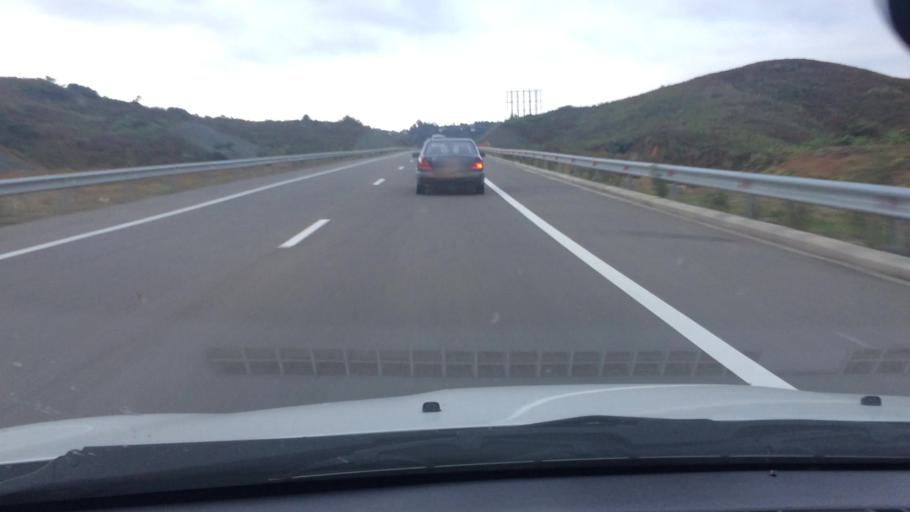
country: GE
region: Ajaria
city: Makhinjauri
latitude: 41.7266
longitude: 41.7502
